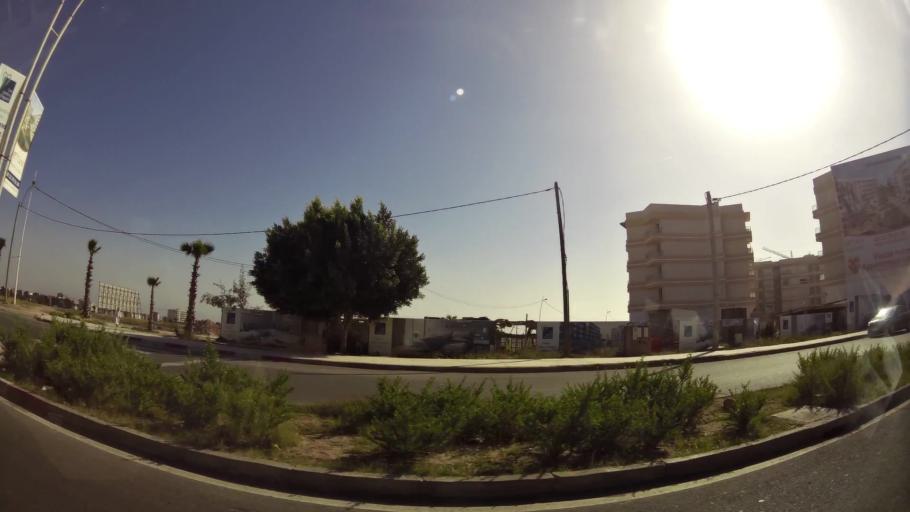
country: MA
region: Oued ed Dahab-Lagouira
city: Dakhla
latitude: 30.4072
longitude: -9.5647
